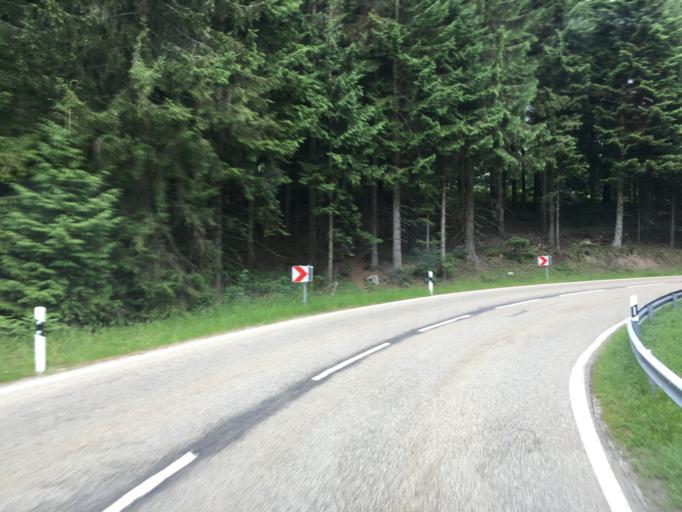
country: DE
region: Baden-Wuerttemberg
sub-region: Karlsruhe Region
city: Buhlertal
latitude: 48.6566
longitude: 8.2393
